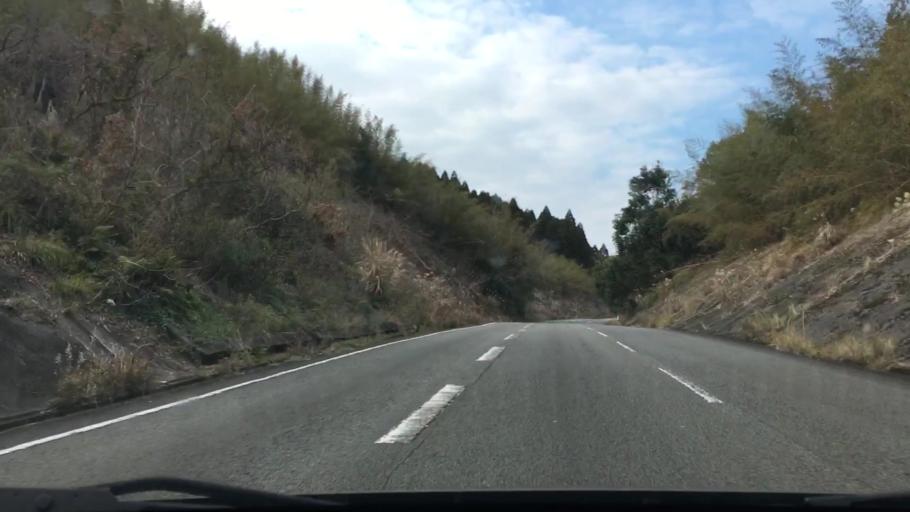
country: JP
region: Miyazaki
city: Nichinan
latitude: 31.6351
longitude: 131.3375
